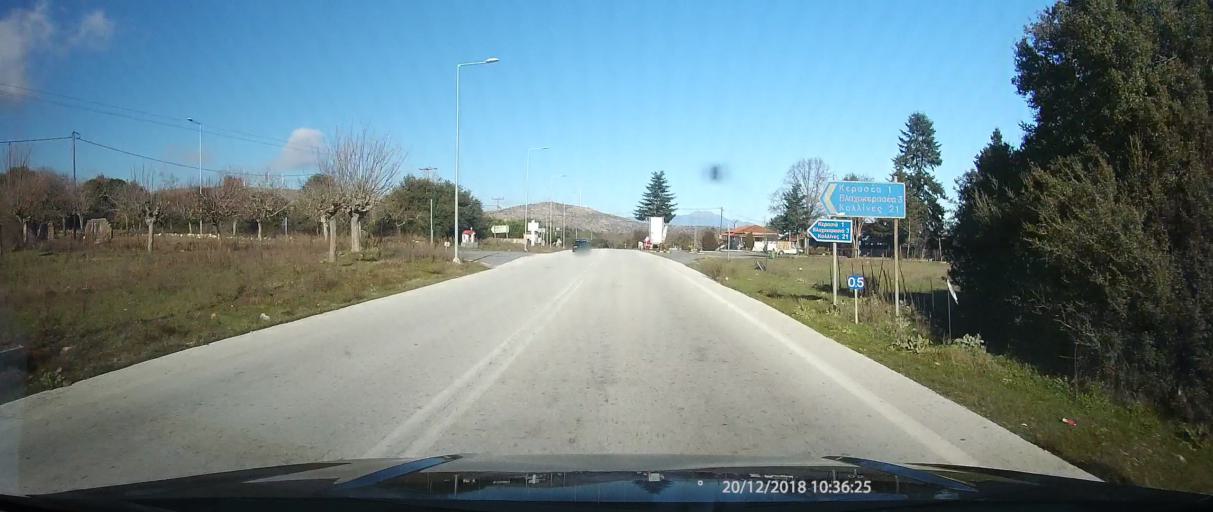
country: GR
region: Peloponnese
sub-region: Nomos Lakonias
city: Kariai
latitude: 37.3659
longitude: 22.4016
